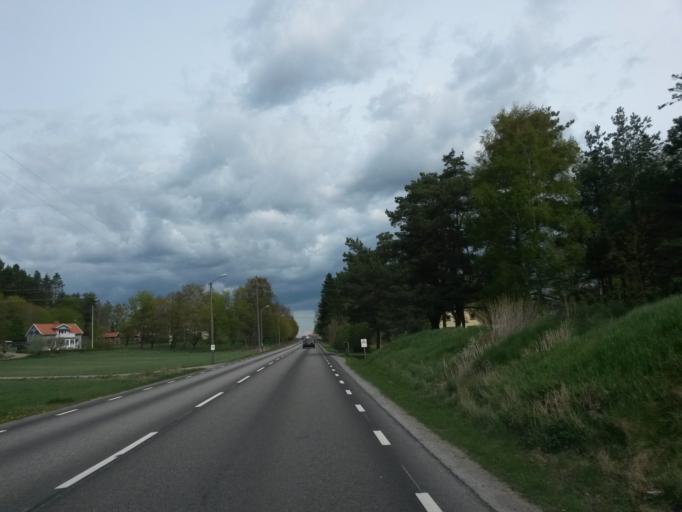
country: SE
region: Vaestra Goetaland
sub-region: Vargarda Kommun
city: Vargarda
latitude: 58.0446
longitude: 12.8145
